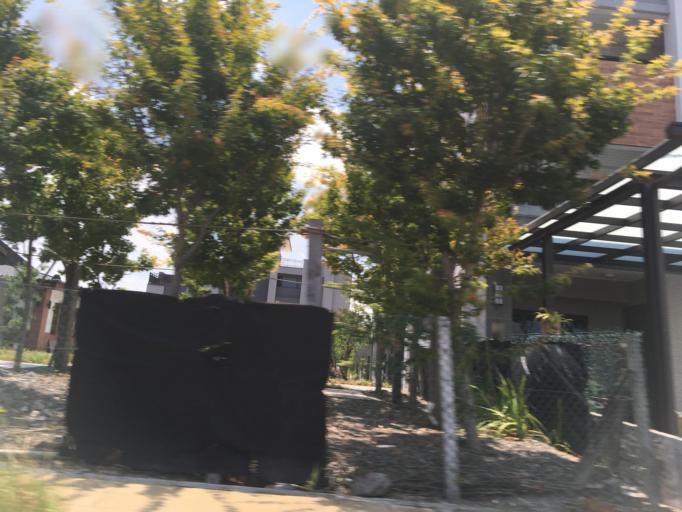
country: TW
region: Taiwan
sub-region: Yilan
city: Yilan
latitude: 24.6594
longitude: 121.7609
